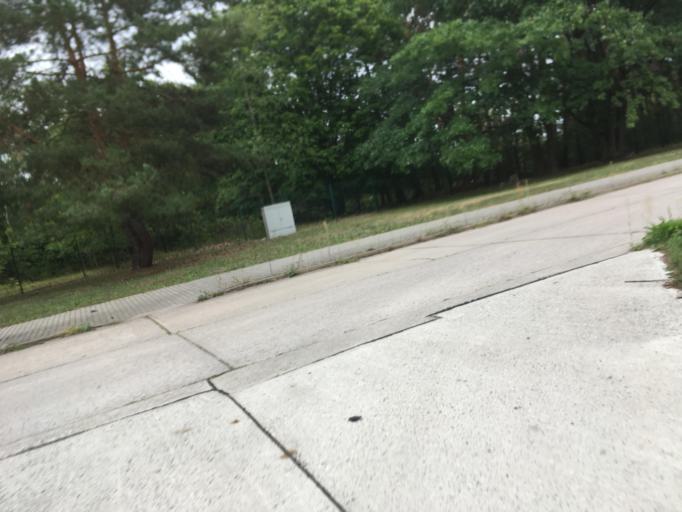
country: DE
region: Brandenburg
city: Meyenburg
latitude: 53.0919
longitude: 14.2215
